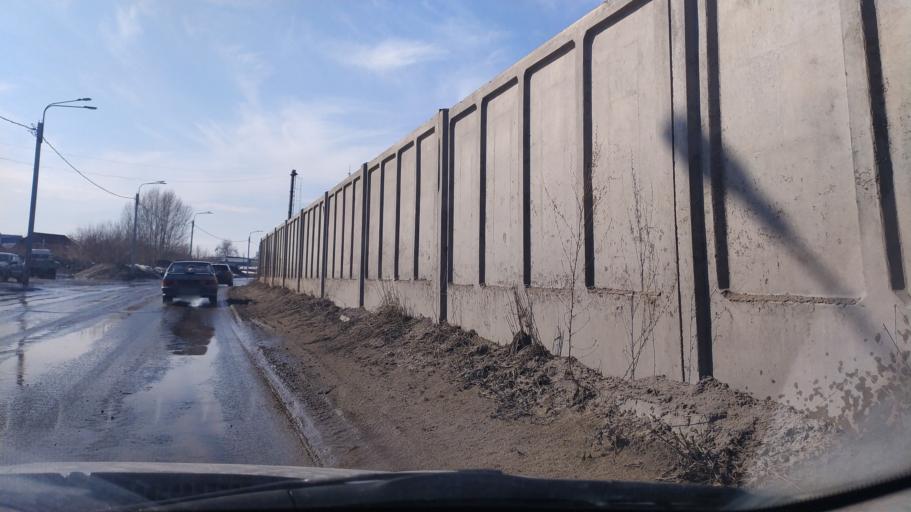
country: RU
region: Chuvashia
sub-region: Cheboksarskiy Rayon
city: Cheboksary
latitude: 56.1173
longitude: 47.2854
